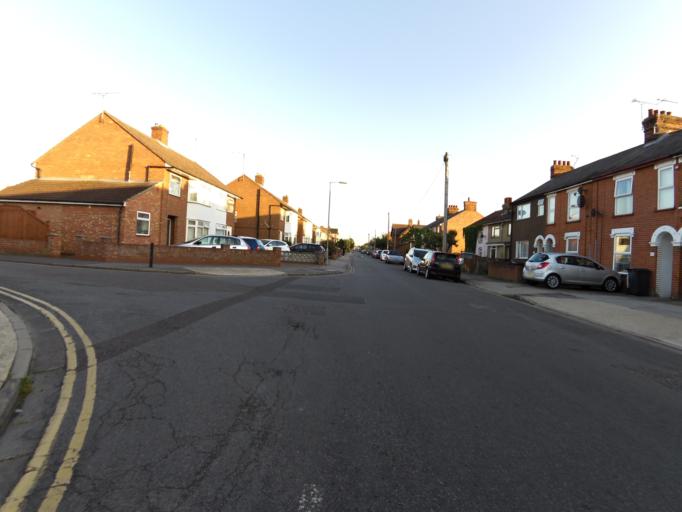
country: GB
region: England
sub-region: Suffolk
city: Ipswich
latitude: 52.0576
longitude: 1.1906
